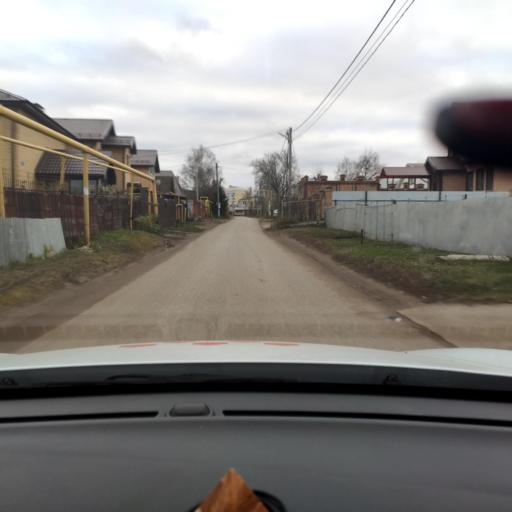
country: RU
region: Tatarstan
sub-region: Gorod Kazan'
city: Kazan
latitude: 55.7924
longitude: 49.2357
